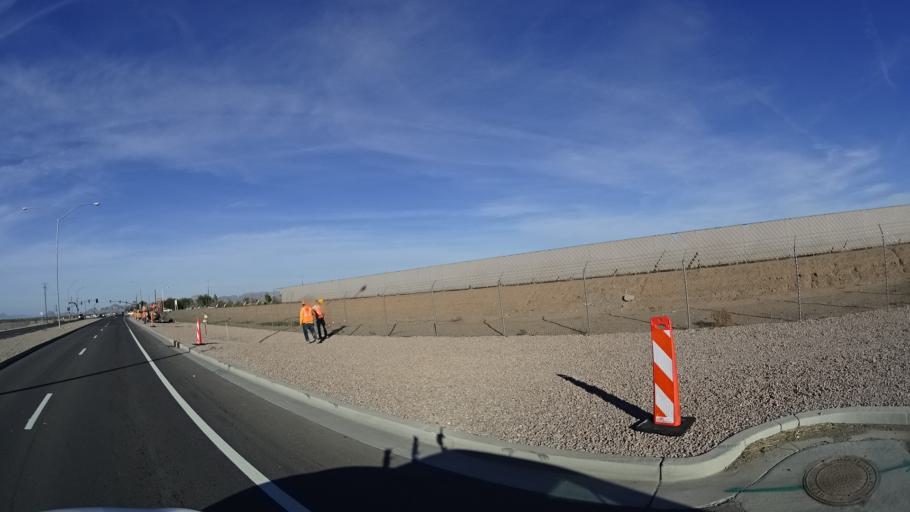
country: US
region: Arizona
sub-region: Maricopa County
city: Queen Creek
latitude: 33.3198
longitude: -111.6354
